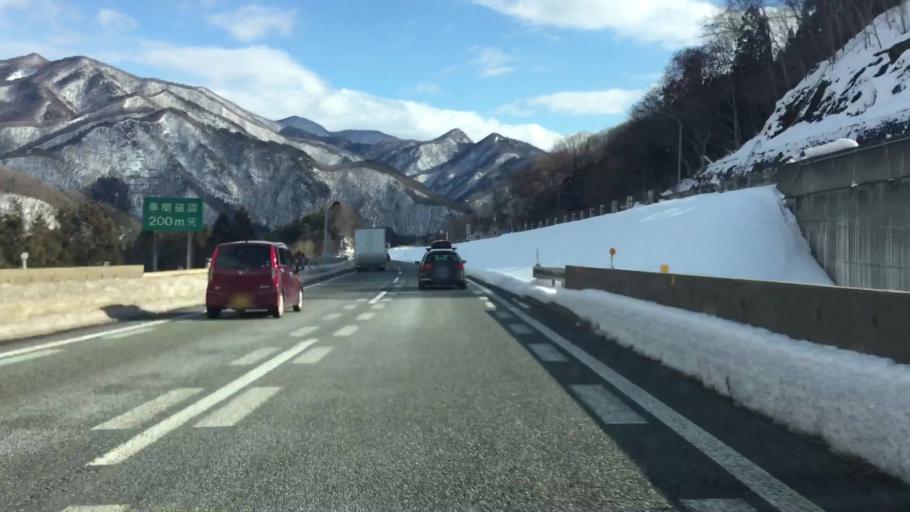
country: JP
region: Gunma
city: Numata
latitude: 36.7734
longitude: 138.9516
